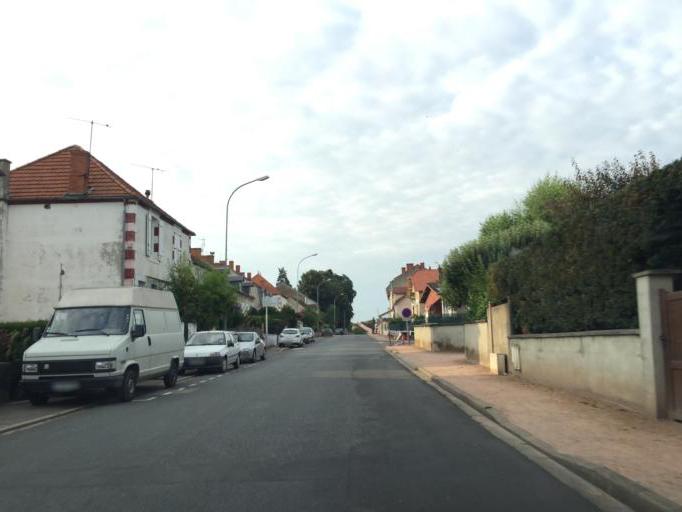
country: FR
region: Auvergne
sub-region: Departement de l'Allier
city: Saint-Germain-des-Fosses
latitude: 46.2111
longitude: 3.4324
